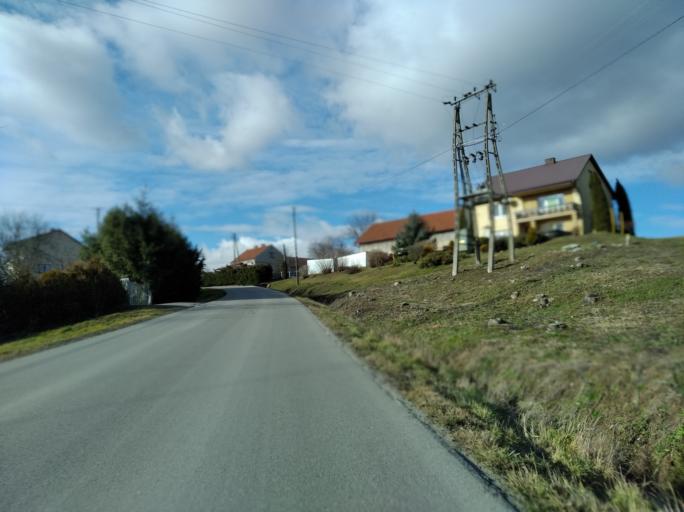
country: PL
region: Subcarpathian Voivodeship
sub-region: Powiat strzyzowski
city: Wisniowa
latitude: 49.9137
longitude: 21.6710
